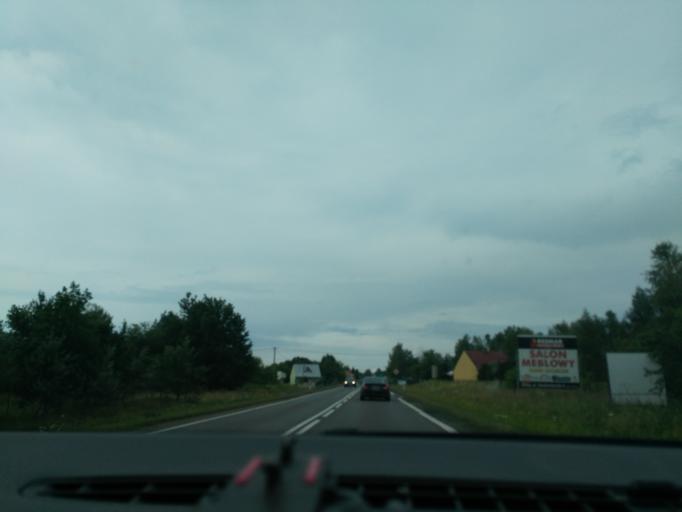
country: PL
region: Subcarpathian Voivodeship
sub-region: Powiat nizanski
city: Nisko
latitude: 50.5127
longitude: 22.1505
